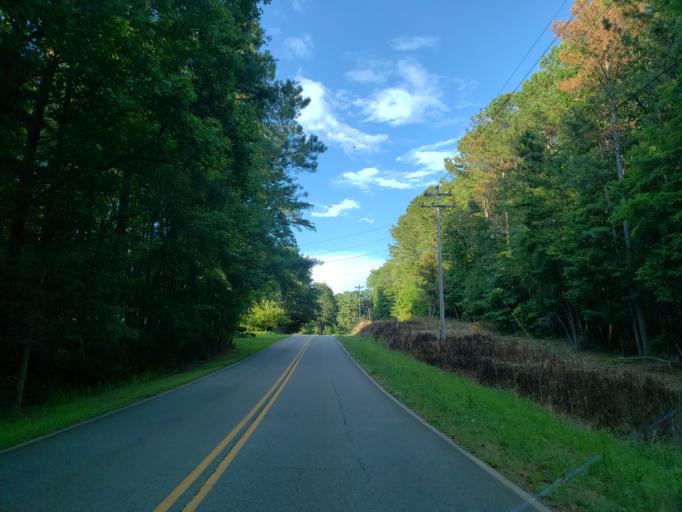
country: US
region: Georgia
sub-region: Cherokee County
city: Canton
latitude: 34.3178
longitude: -84.5285
